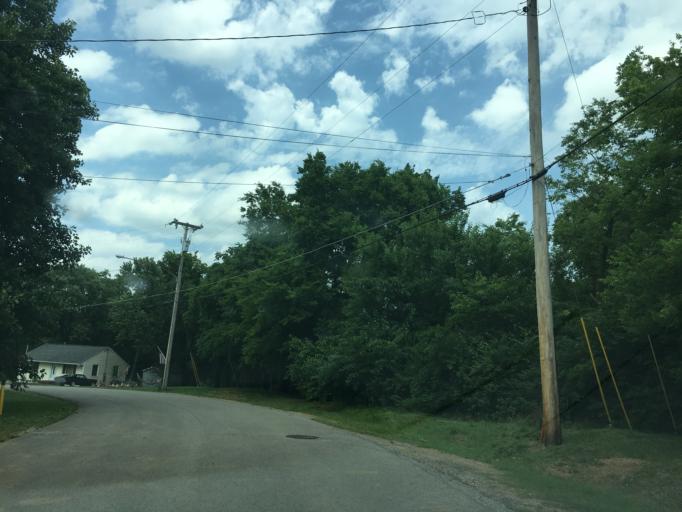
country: US
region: Tennessee
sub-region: Davidson County
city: Nashville
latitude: 36.1295
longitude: -86.7483
